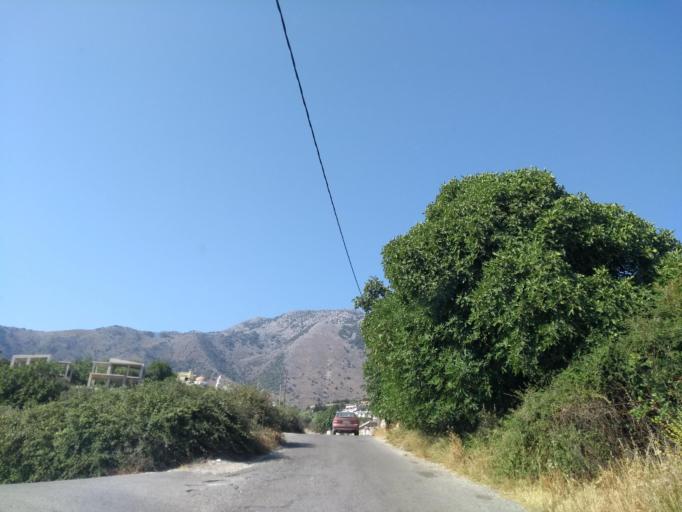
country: GR
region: Crete
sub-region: Nomos Chanias
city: Georgioupolis
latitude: 35.3176
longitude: 24.2962
